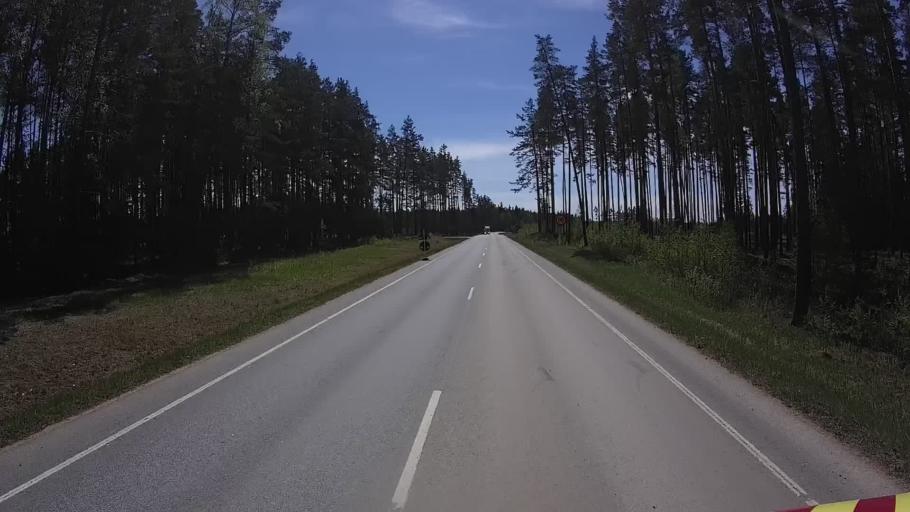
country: EE
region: Polvamaa
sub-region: Polva linn
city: Polva
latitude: 57.9241
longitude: 27.1825
